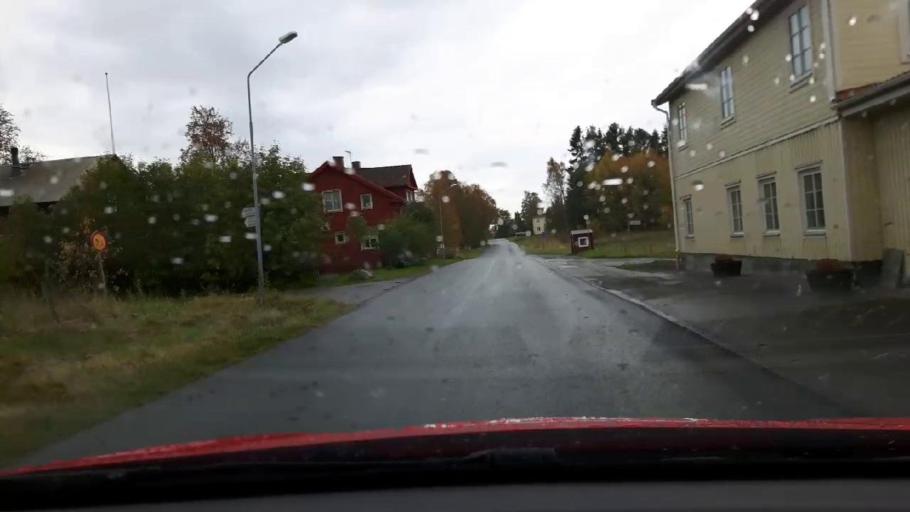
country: SE
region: Jaemtland
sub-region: Bergs Kommun
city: Hoverberg
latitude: 62.9259
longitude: 14.5160
